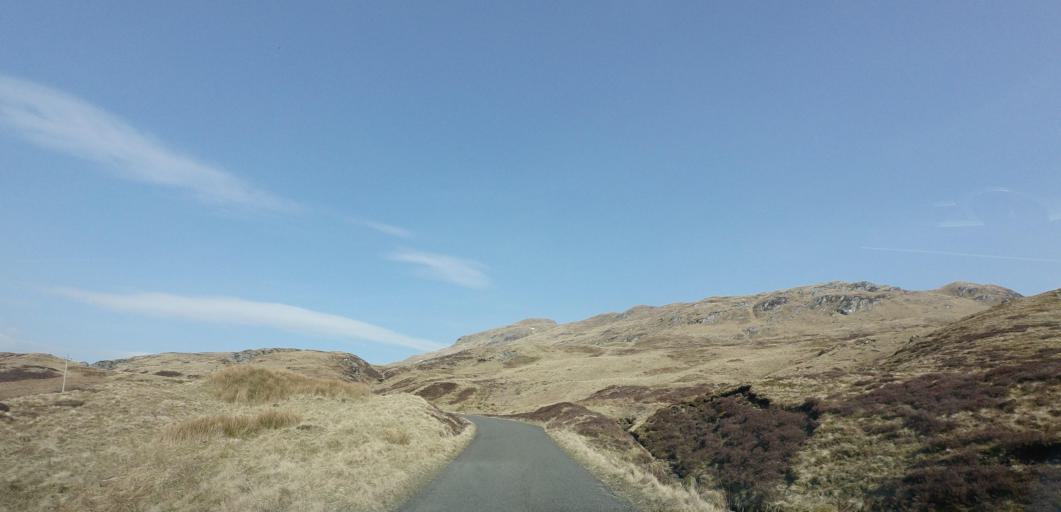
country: GB
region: Scotland
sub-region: Stirling
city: Callander
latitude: 56.5193
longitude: -4.2731
